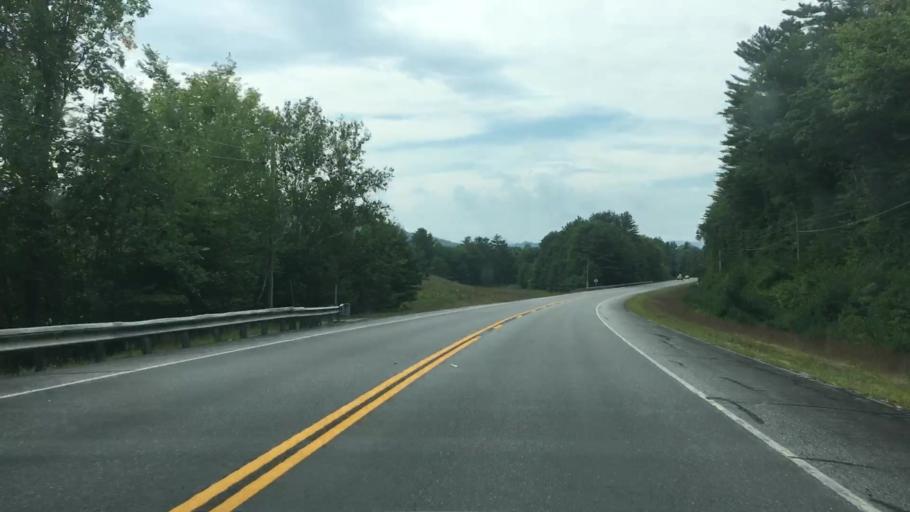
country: US
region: Maine
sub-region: Oxford County
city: Bethel
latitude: 44.4862
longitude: -70.7643
